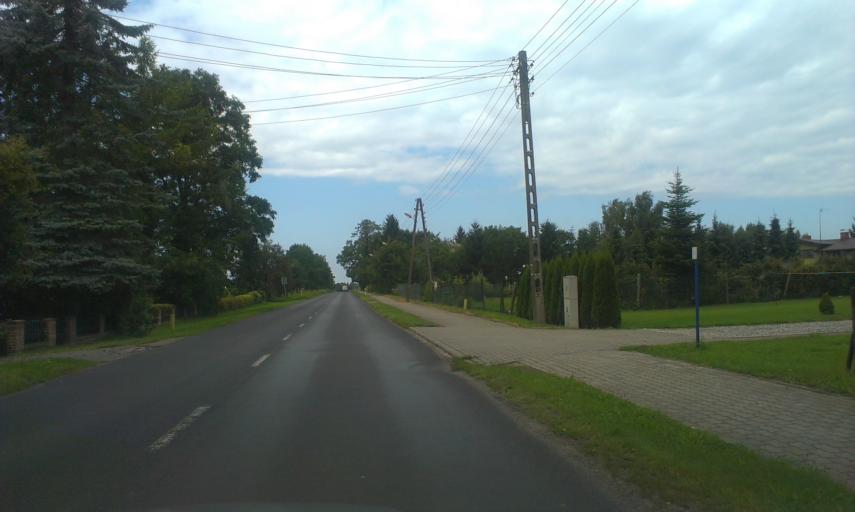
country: PL
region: West Pomeranian Voivodeship
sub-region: Powiat kolobrzeski
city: Dygowo
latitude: 54.1332
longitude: 15.7147
